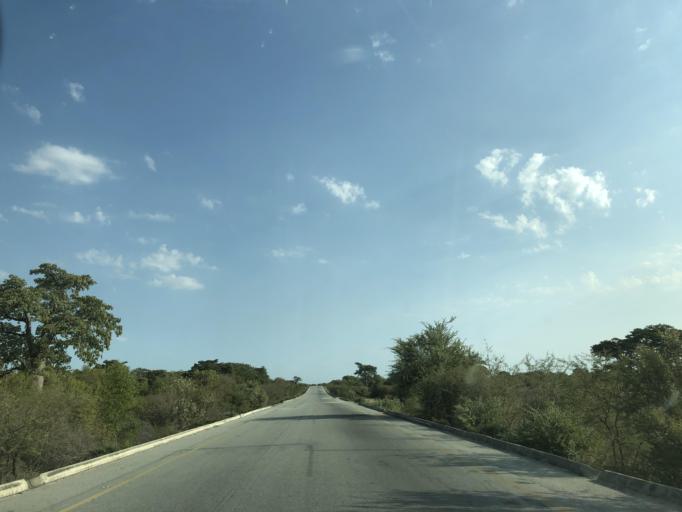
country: AO
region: Benguela
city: Benguela
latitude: -13.2017
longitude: 13.7633
